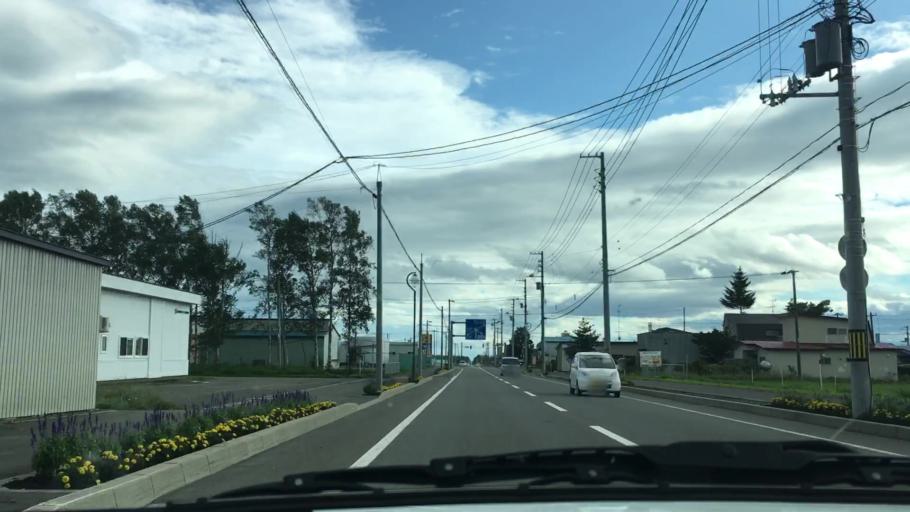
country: JP
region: Hokkaido
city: Otofuke
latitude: 43.2272
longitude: 143.2938
